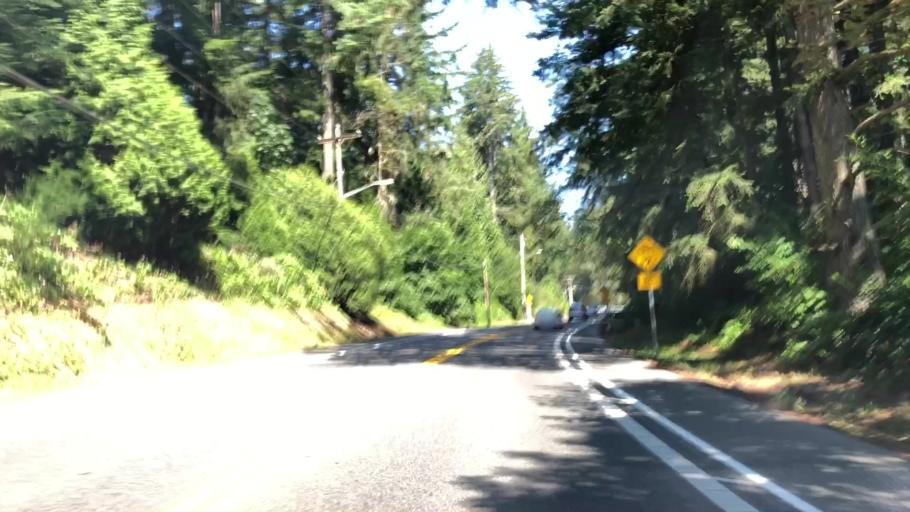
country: US
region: Washington
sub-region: King County
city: Inglewood-Finn Hill
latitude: 47.7224
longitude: -122.2400
